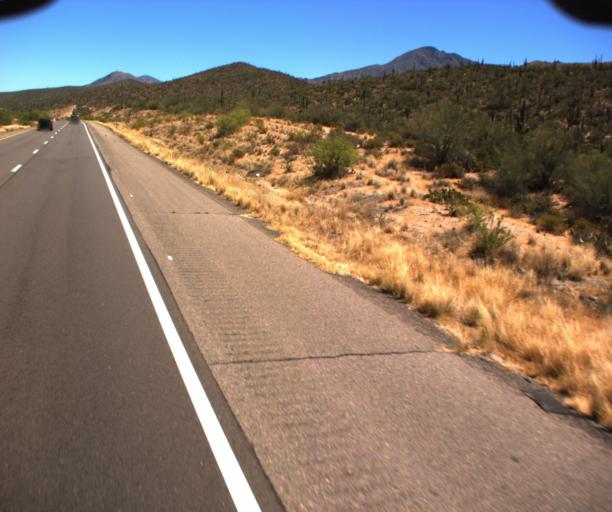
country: US
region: Arizona
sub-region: Maricopa County
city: Rio Verde
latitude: 33.7570
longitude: -111.4965
